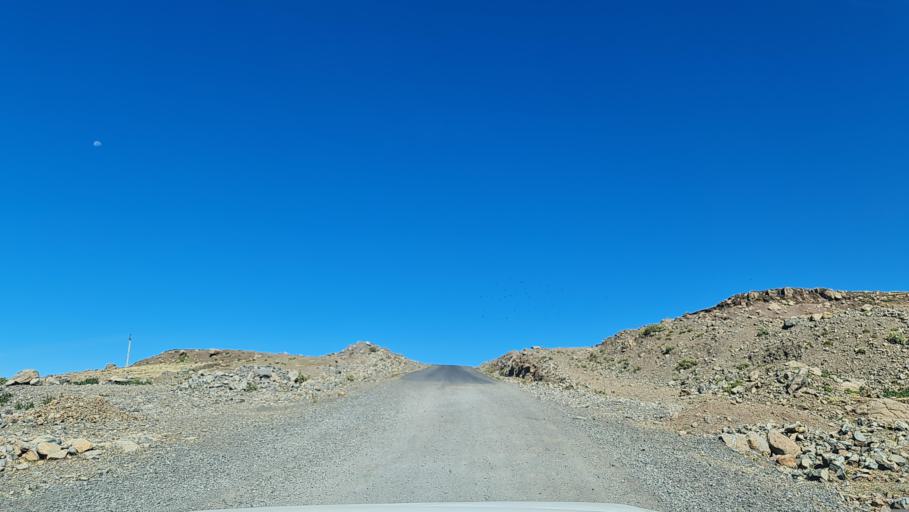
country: ET
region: Amhara
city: Debark'
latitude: 13.1528
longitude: 38.1878
